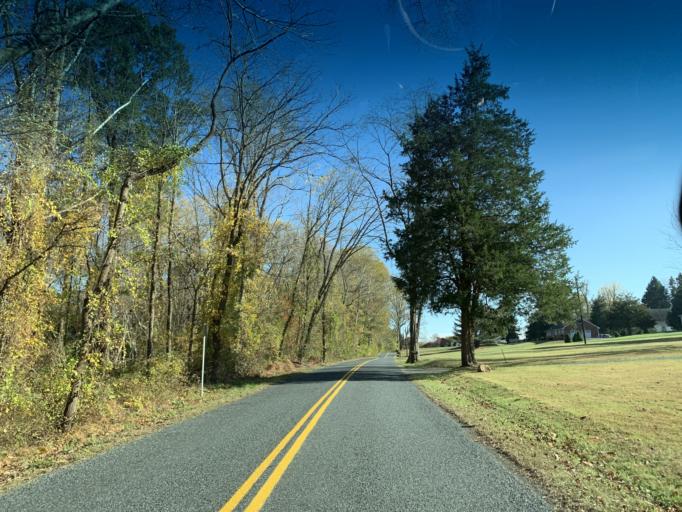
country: US
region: Maryland
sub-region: Harford County
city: Joppatowne
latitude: 39.4784
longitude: -76.3437
